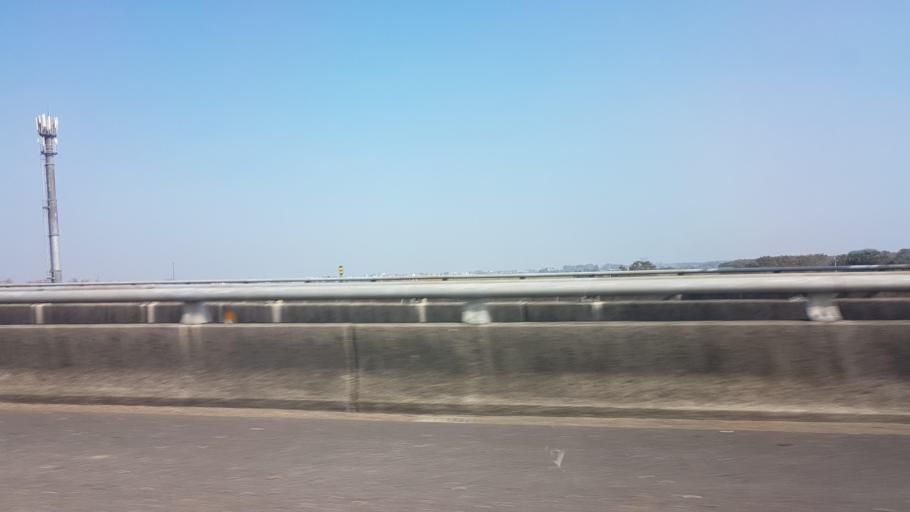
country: TW
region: Taiwan
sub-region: Chiayi
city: Taibao
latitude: 23.4237
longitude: 120.3605
